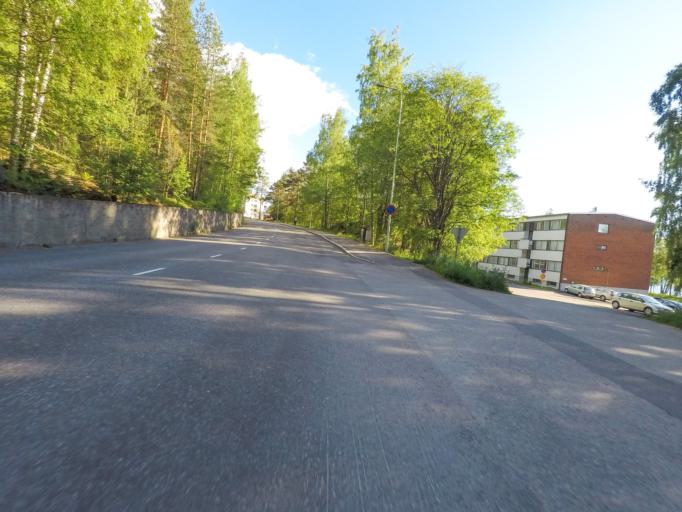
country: FI
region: Southern Savonia
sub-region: Savonlinna
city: Savonlinna
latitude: 61.8671
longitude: 28.8561
